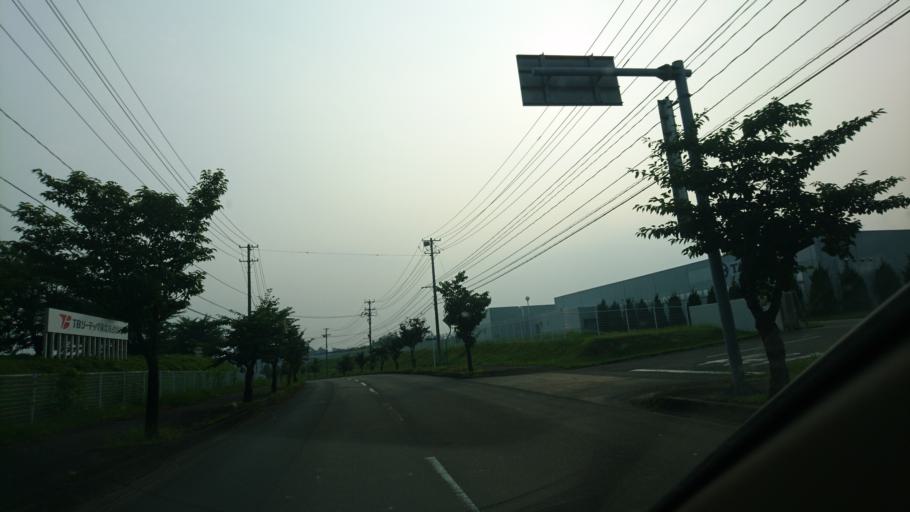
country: JP
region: Iwate
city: Mizusawa
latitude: 39.2119
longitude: 141.1818
